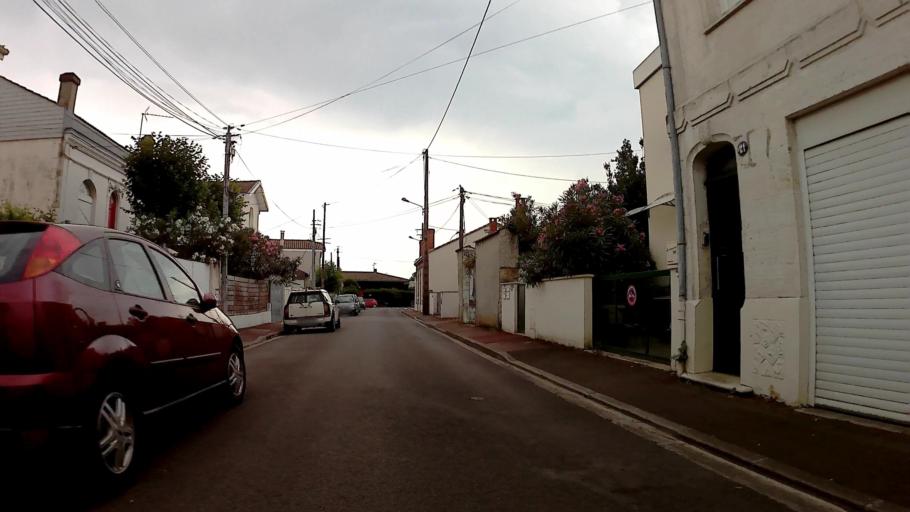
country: FR
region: Aquitaine
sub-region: Departement de la Gironde
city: Le Bouscat
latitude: 44.8659
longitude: -0.5891
